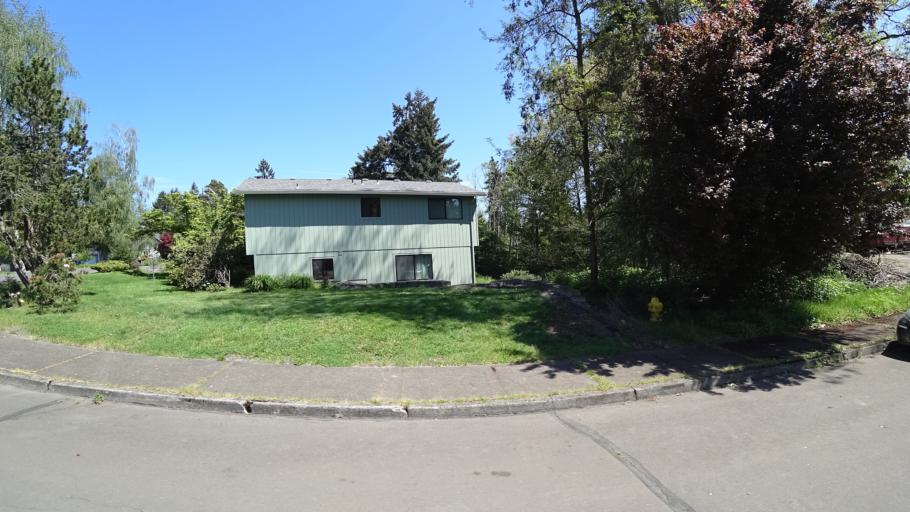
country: US
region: Oregon
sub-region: Washington County
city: Hillsboro
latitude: 45.5152
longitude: -122.9621
